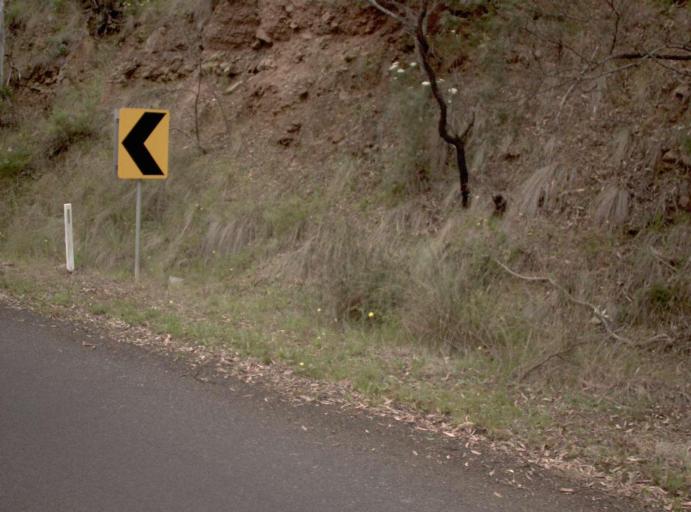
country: AU
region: Victoria
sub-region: East Gippsland
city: Bairnsdale
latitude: -37.4843
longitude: 147.2063
